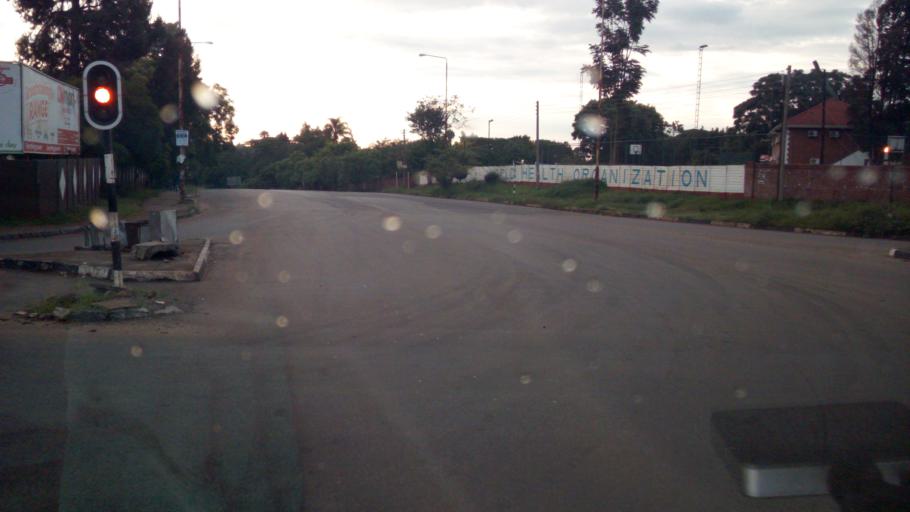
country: ZW
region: Harare
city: Harare
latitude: -17.8011
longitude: 31.0882
